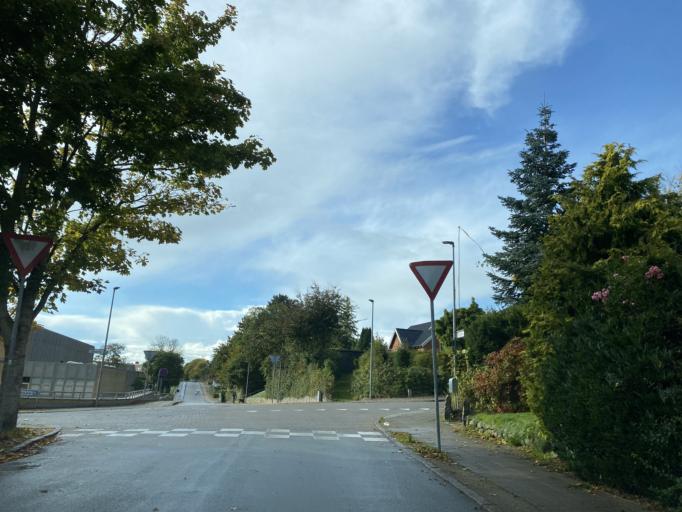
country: DK
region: South Denmark
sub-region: Haderslev Kommune
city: Haderslev
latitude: 55.2568
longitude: 9.4878
